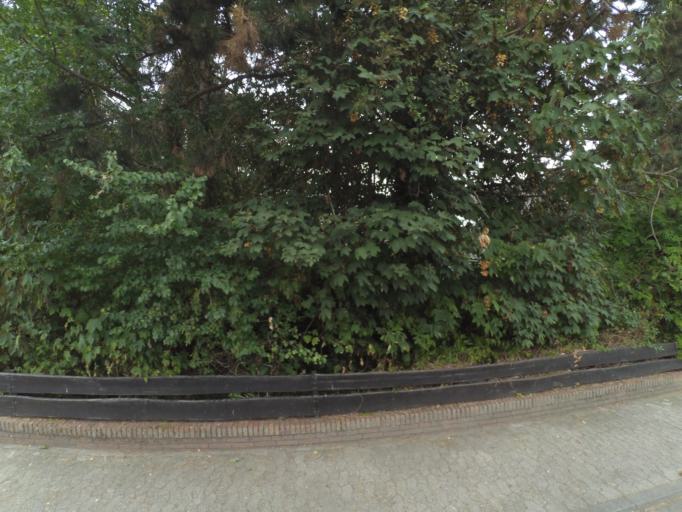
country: DE
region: Hesse
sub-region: Regierungsbezirk Darmstadt
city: Einhausen
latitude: 49.6963
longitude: 8.5742
